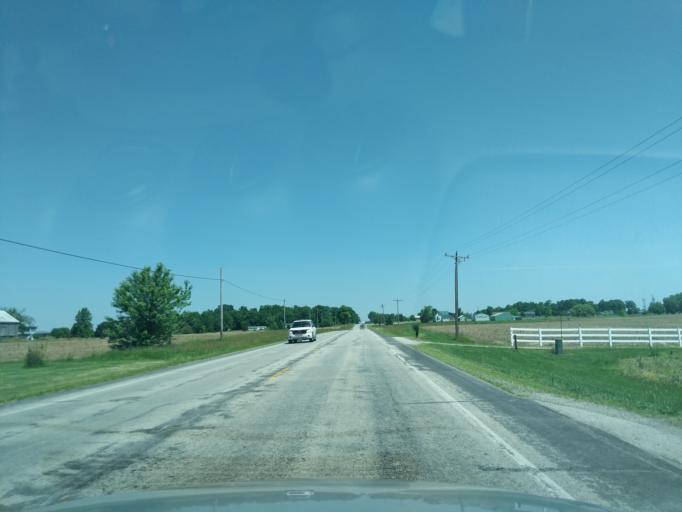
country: US
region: Indiana
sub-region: Whitley County
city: Columbia City
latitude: 41.0962
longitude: -85.4714
